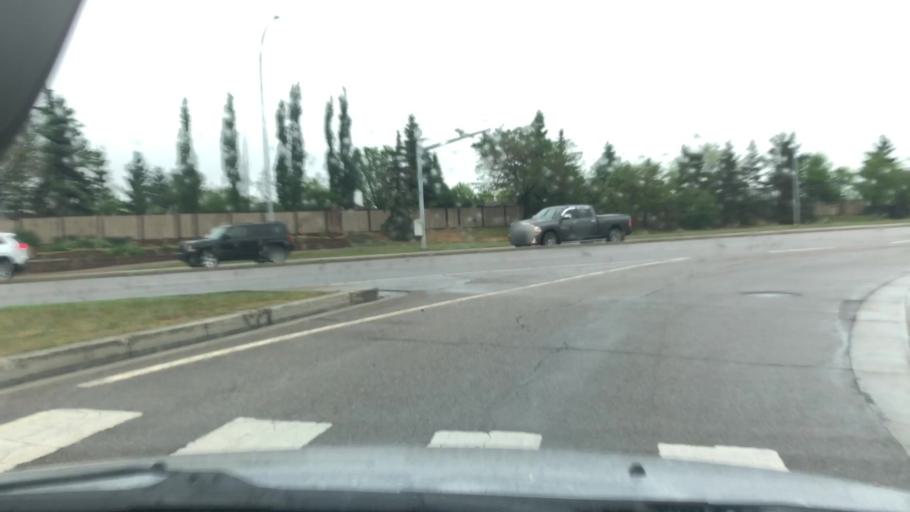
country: CA
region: Alberta
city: Sherwood Park
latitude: 53.5410
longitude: -113.2631
